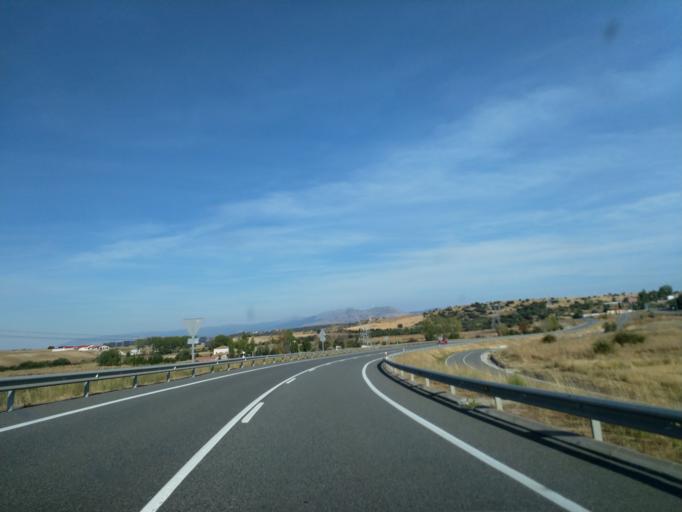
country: ES
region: Castille and Leon
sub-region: Provincia de Segovia
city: Villacastin
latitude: 40.7845
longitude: -4.4189
